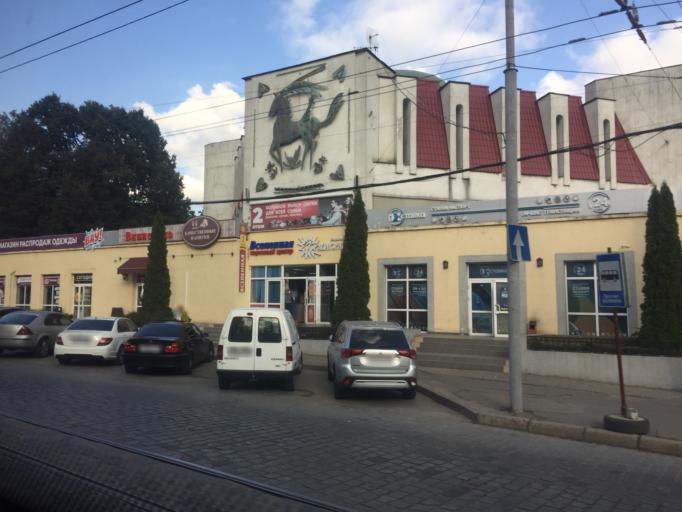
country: RU
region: Kaliningrad
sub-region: Gorod Kaliningrad
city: Kaliningrad
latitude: 54.6959
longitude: 20.5032
